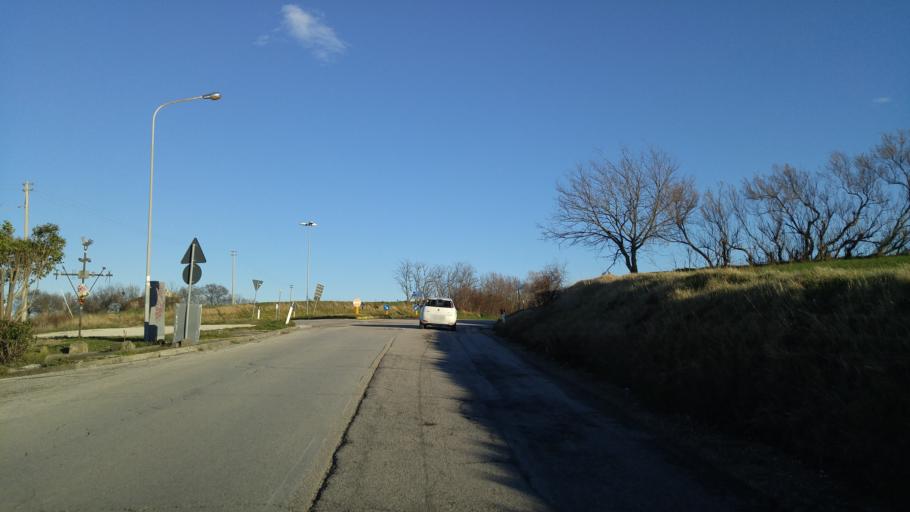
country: IT
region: The Marches
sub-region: Provincia di Pesaro e Urbino
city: San Costanzo
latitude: 43.7669
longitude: 13.0870
